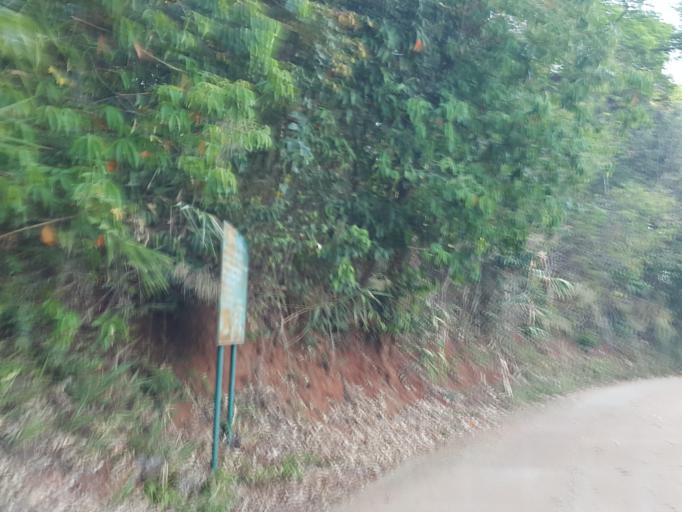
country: TH
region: Chiang Mai
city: Samoeng
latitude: 18.9074
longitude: 98.7974
